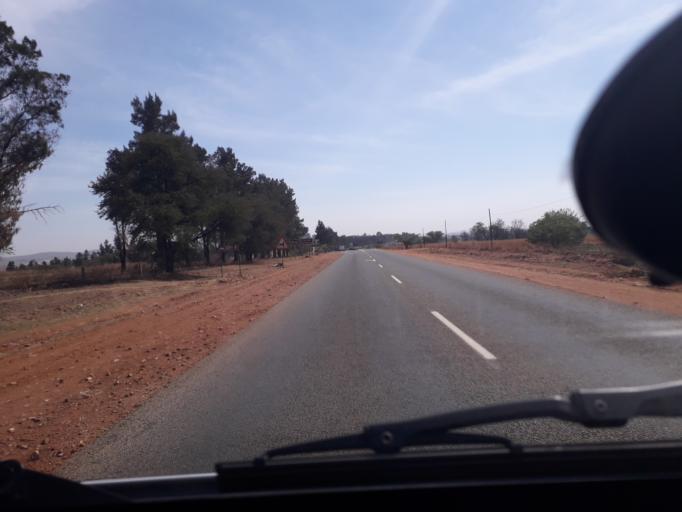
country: ZA
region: Gauteng
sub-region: West Rand District Municipality
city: Muldersdriseloop
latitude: -25.9970
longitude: 27.8574
